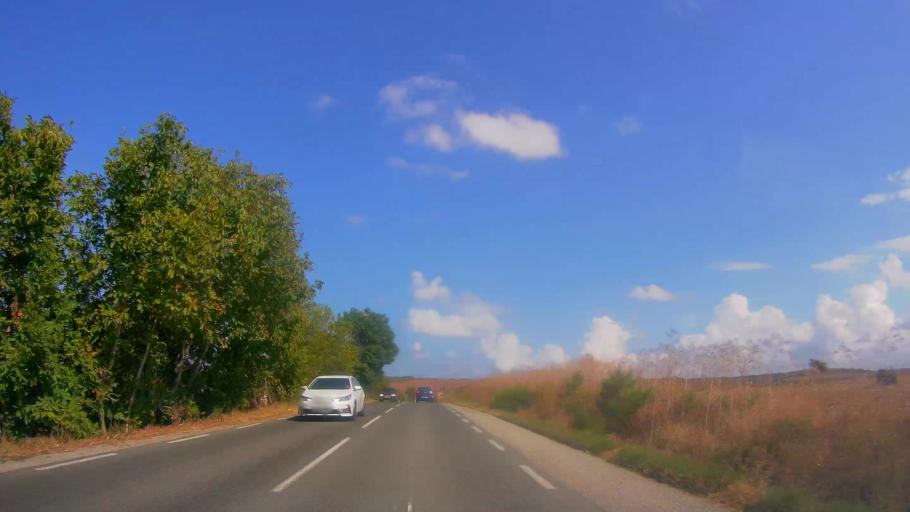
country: BG
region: Burgas
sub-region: Obshtina Burgas
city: Burgas
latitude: 42.4808
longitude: 27.3780
